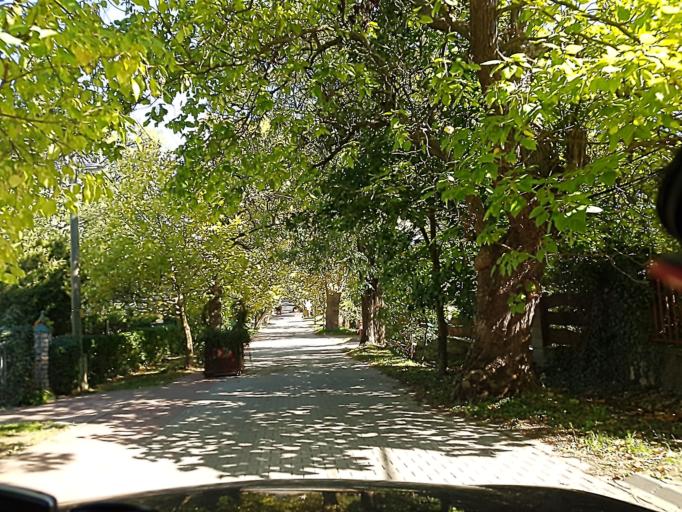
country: HU
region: Pest
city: Piliscsaba
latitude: 47.6364
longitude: 18.8399
